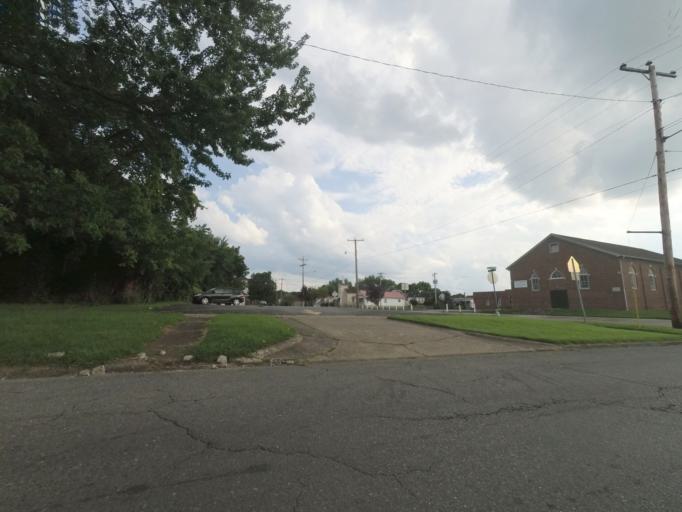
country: US
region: West Virginia
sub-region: Cabell County
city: Huntington
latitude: 38.4305
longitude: -82.4100
